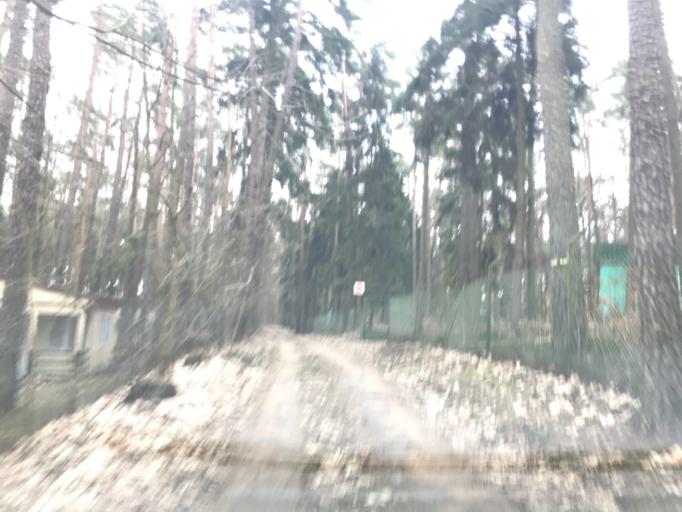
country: PL
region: Warmian-Masurian Voivodeship
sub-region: Powiat dzialdowski
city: Lidzbark
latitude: 53.2568
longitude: 19.8066
